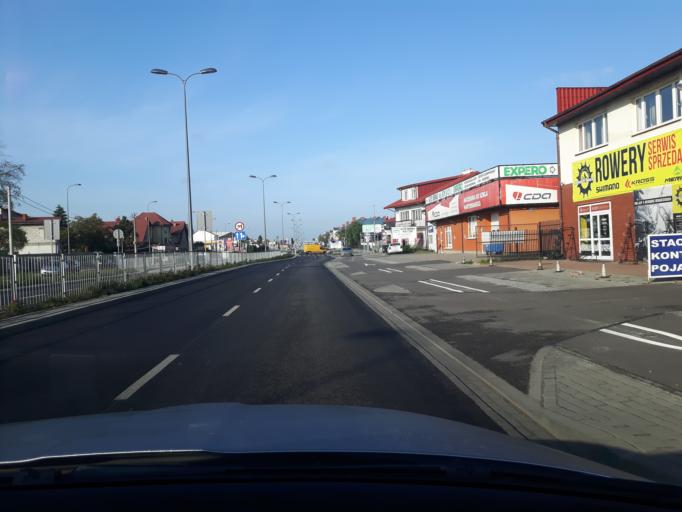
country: PL
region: Masovian Voivodeship
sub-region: Powiat wolominski
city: Zabki
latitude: 52.2864
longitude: 21.0906
